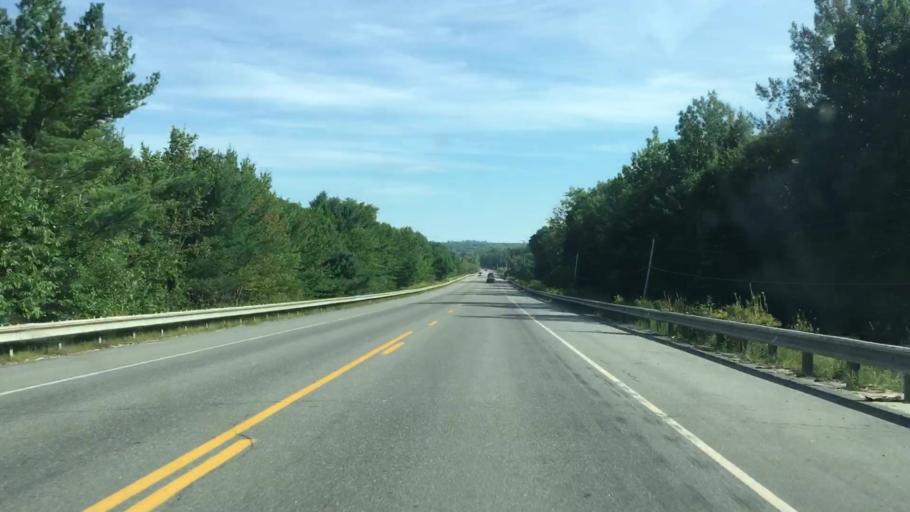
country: US
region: Maine
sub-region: Penobscot County
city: Lincoln
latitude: 45.3667
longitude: -68.5523
